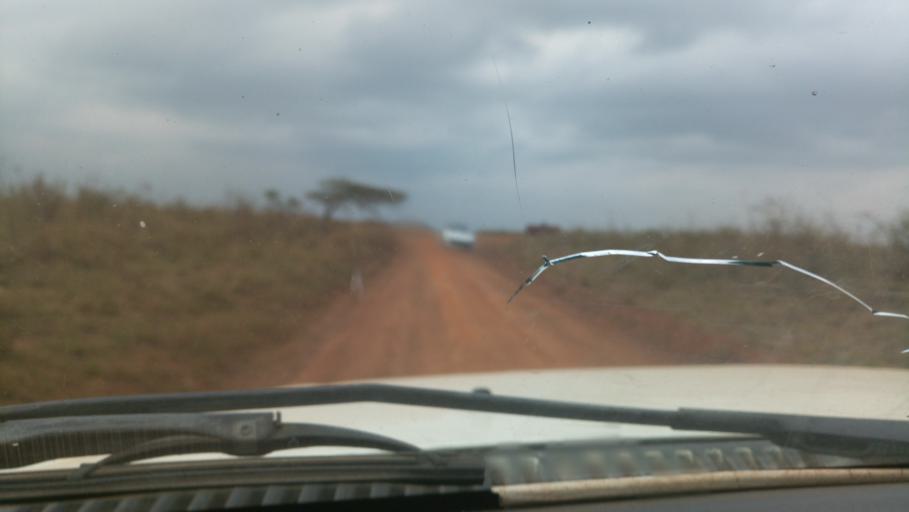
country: KE
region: Nairobi Area
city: Nairobi
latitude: -1.3493
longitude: 36.8223
